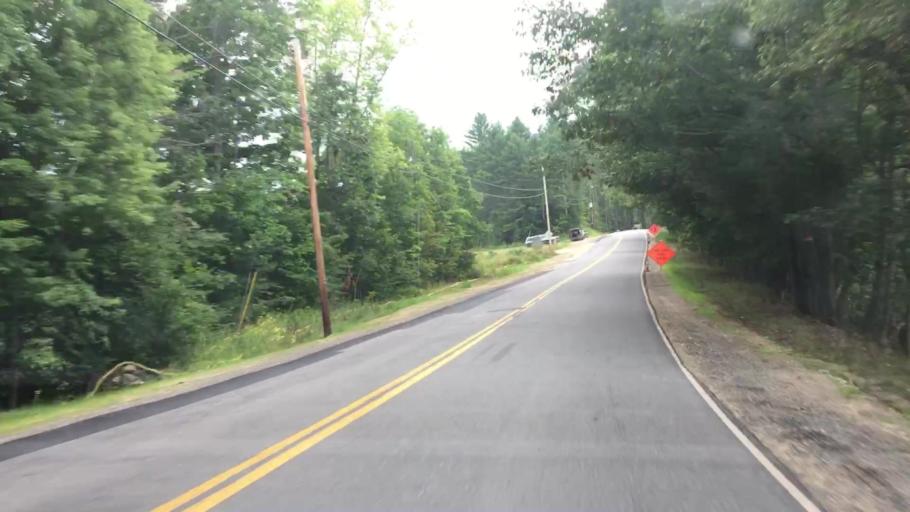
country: US
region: Maine
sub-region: Oxford County
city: Rumford
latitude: 44.5227
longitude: -70.6802
